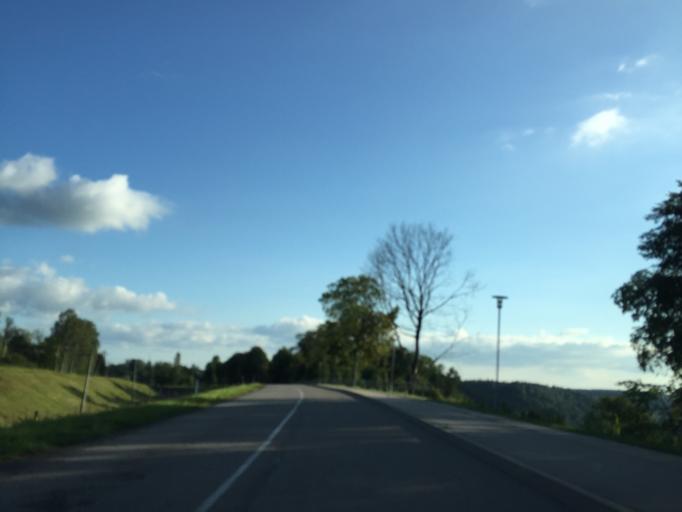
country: LV
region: Sigulda
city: Sigulda
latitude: 57.1499
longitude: 24.8401
